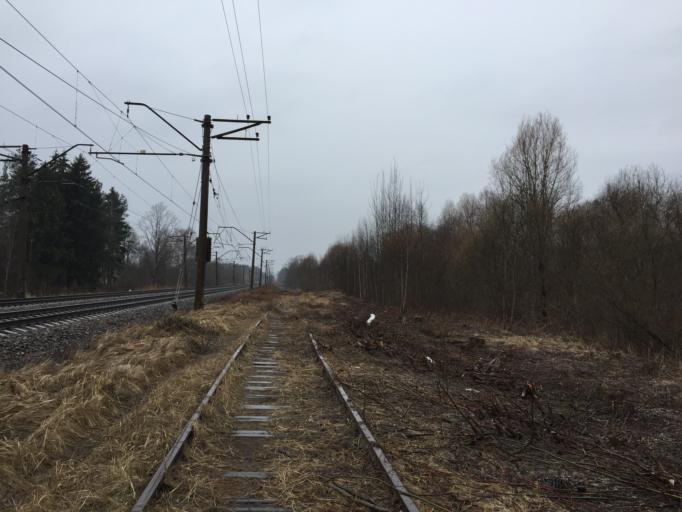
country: LV
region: Lielvarde
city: Lielvarde
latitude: 56.7252
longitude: 24.7841
